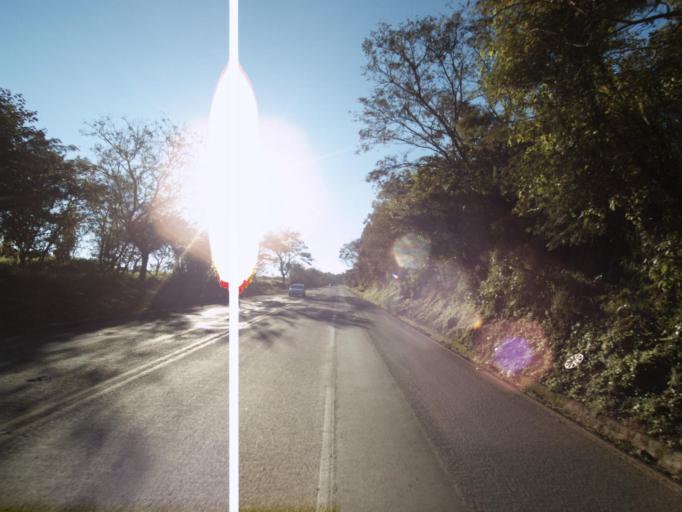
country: BR
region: Santa Catarina
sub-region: Chapeco
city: Chapeco
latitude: -26.9198
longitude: -52.8613
